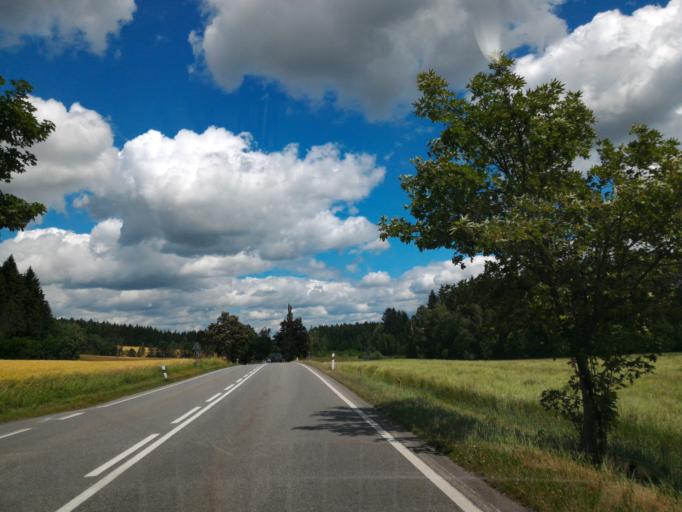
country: CZ
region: Vysocina
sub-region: Okres Jihlava
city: Trest'
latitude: 49.2416
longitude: 15.4649
